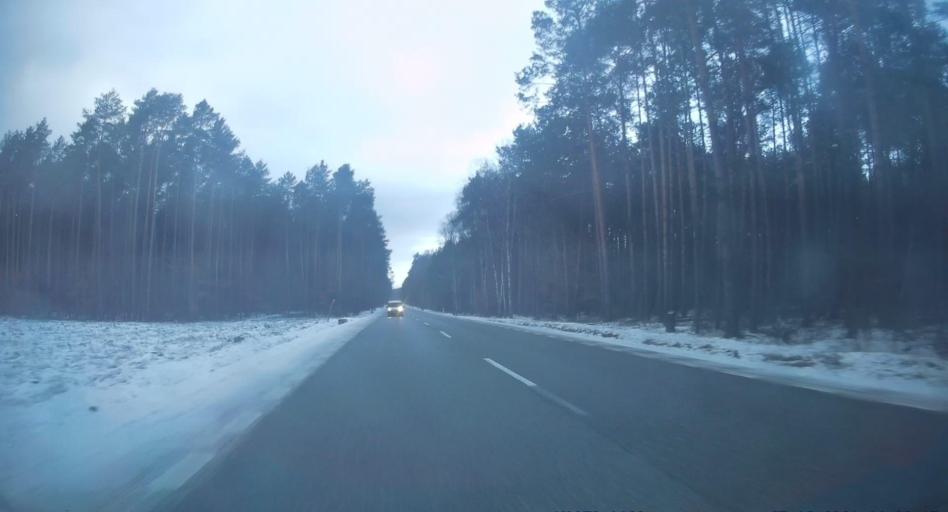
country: PL
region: Swietokrzyskie
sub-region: Powiat konecki
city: Smykow
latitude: 51.0917
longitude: 20.3535
